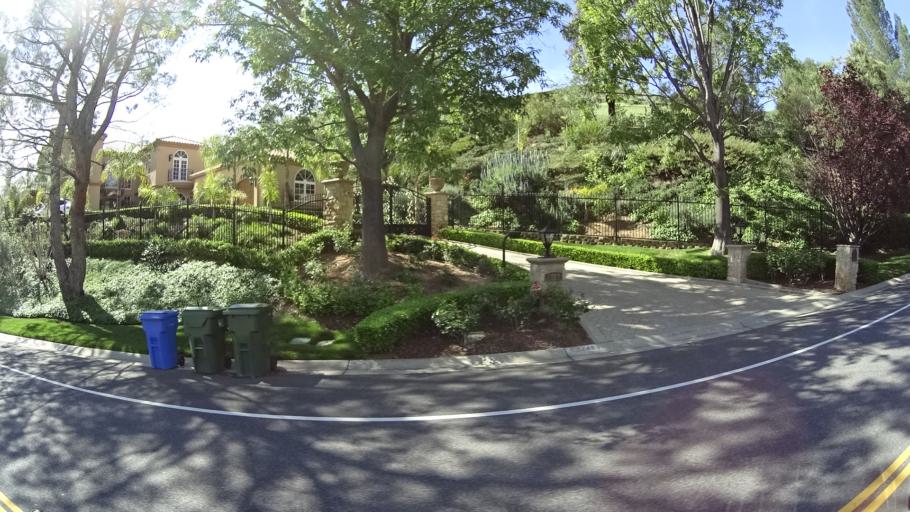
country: US
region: California
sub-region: Ventura County
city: Oak Park
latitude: 34.1872
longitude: -118.7986
